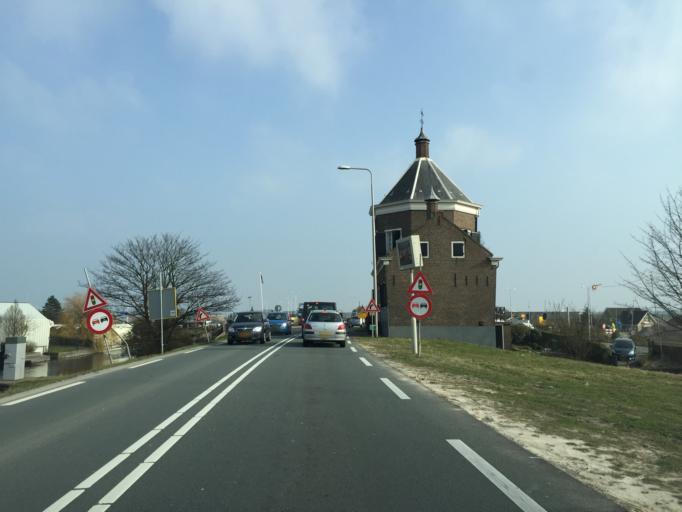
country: NL
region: South Holland
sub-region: Gemeente Westland
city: Maasdijk
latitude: 51.9709
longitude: 4.2022
